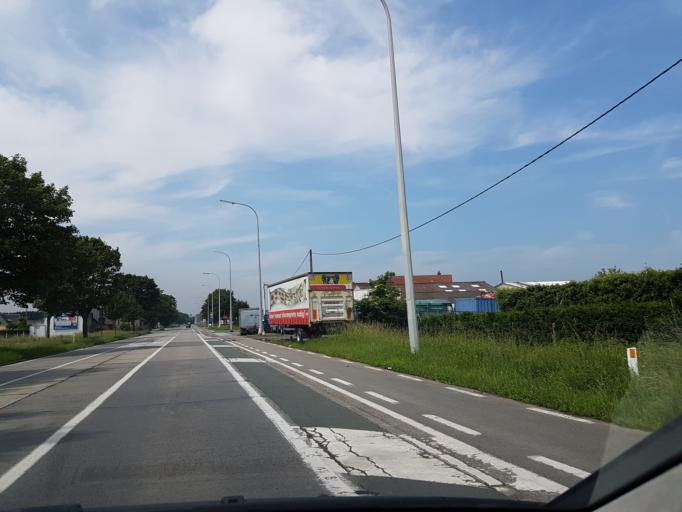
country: BE
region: Flanders
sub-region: Provincie Vlaams-Brabant
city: Ternat
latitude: 50.9143
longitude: 4.1436
